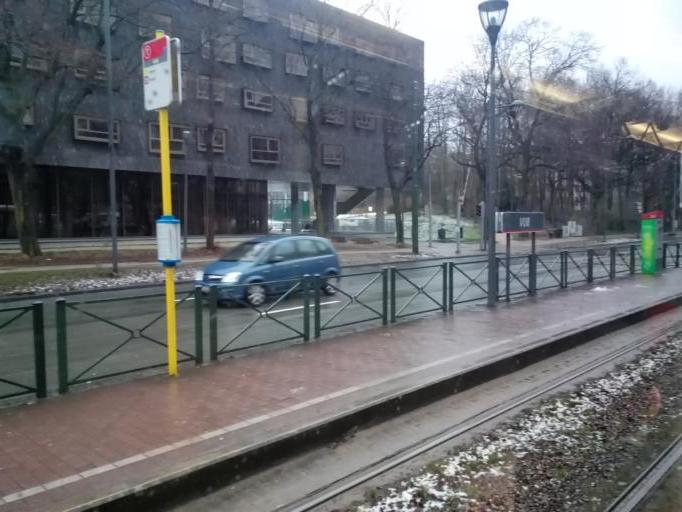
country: BE
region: Brussels Capital
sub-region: Bruxelles-Capitale
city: Brussels
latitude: 50.8246
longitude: 4.3938
